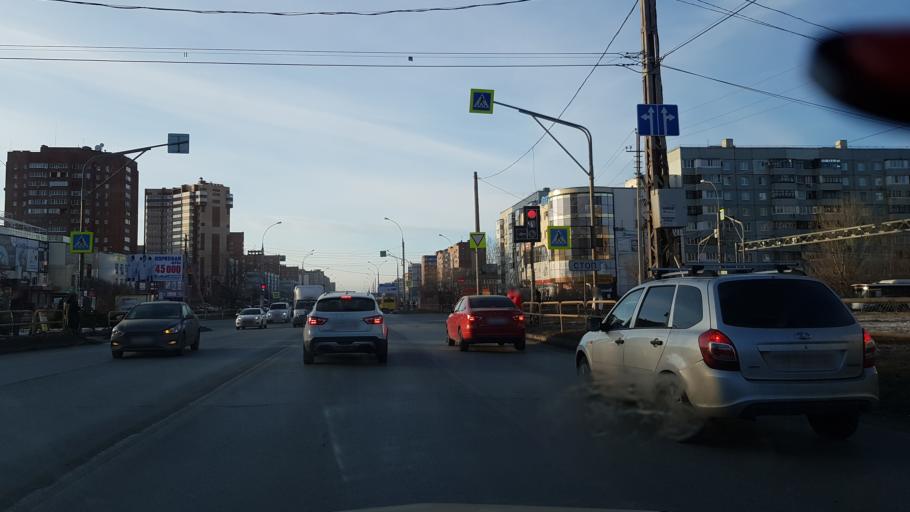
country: RU
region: Samara
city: Tol'yatti
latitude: 53.5410
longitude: 49.3466
